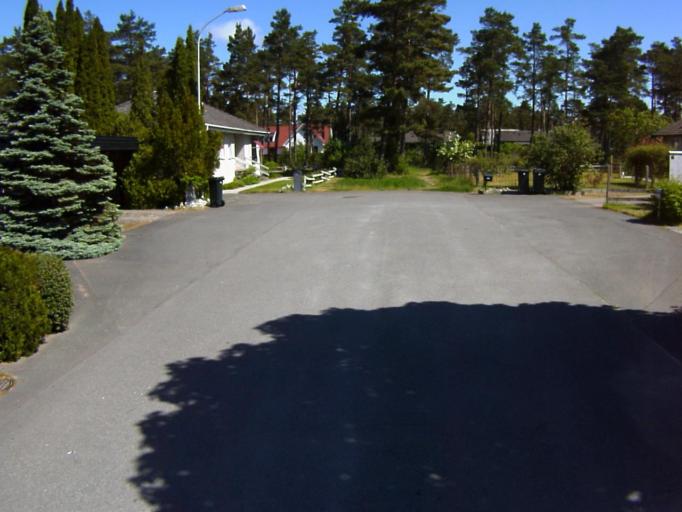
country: SE
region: Skane
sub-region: Kristianstads Kommun
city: Ahus
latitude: 55.9427
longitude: 14.2939
